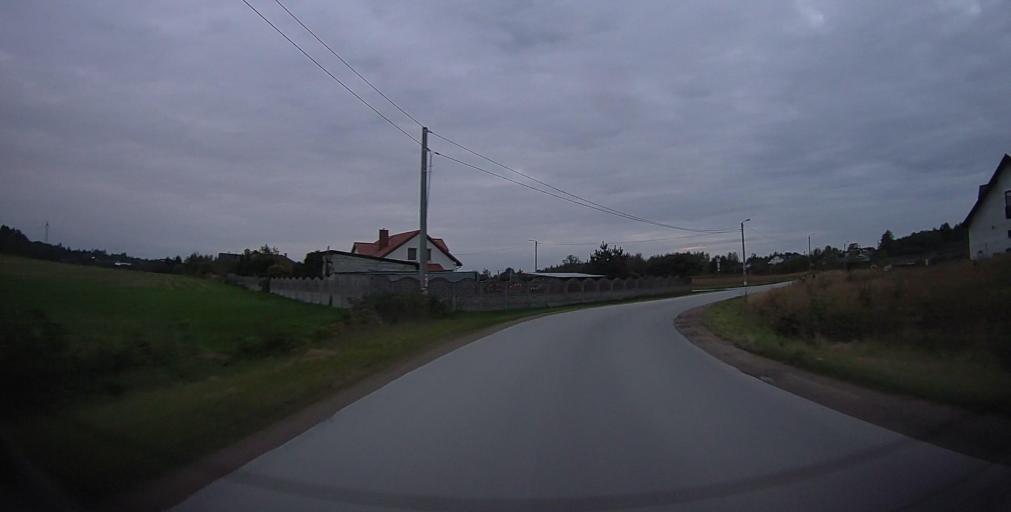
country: PL
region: Masovian Voivodeship
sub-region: Powiat radomski
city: Jedlinsk
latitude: 51.4606
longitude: 21.1240
